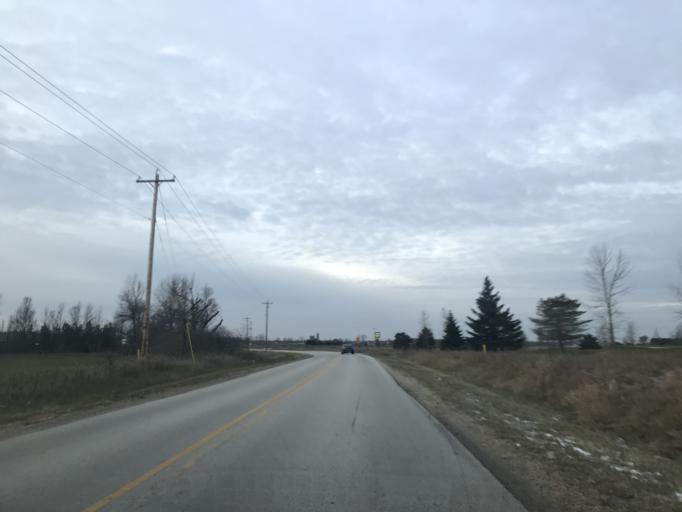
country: US
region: Wisconsin
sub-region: Marinette County
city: Peshtigo
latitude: 45.0540
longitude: -87.7993
